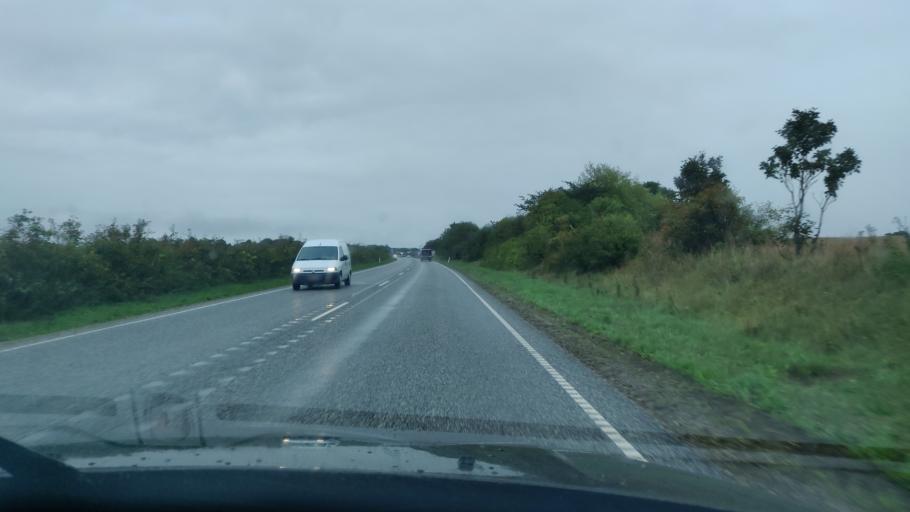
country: DK
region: North Denmark
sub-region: Thisted Kommune
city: Thisted
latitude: 56.9706
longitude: 8.7281
